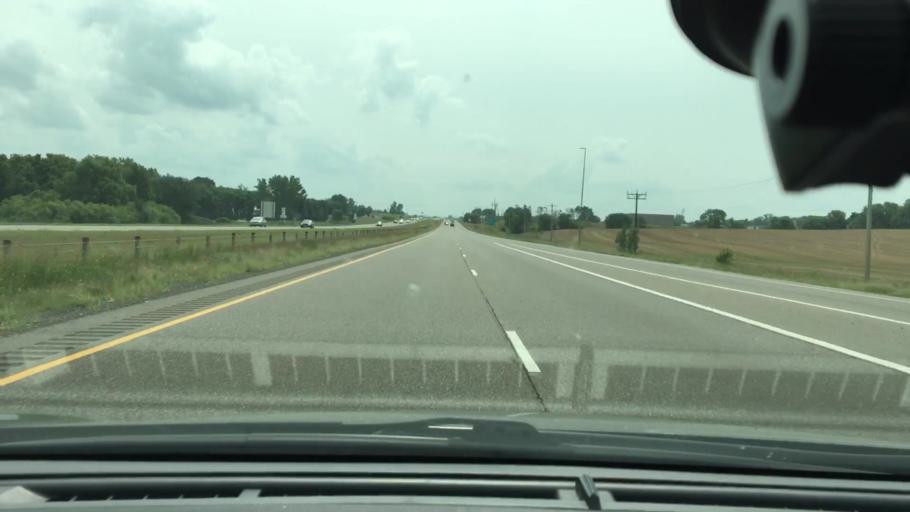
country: US
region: Minnesota
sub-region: Hennepin County
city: Rogers
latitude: 45.2254
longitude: -93.5527
